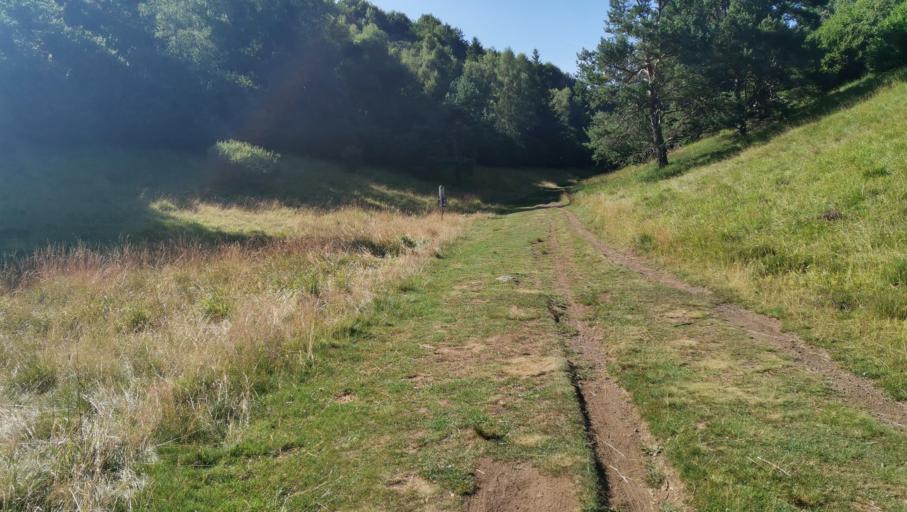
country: FR
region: Auvergne
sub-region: Departement du Puy-de-Dome
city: Orcines
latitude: 45.7948
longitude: 2.9653
